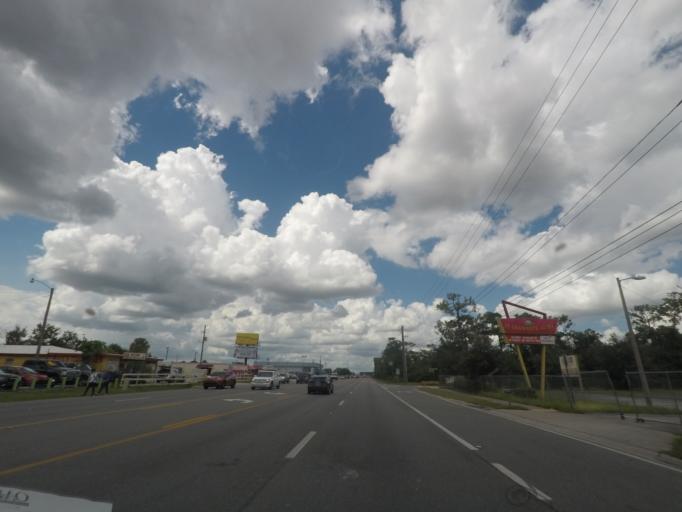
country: US
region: Florida
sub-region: Osceola County
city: Kissimmee
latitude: 28.3295
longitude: -81.4037
